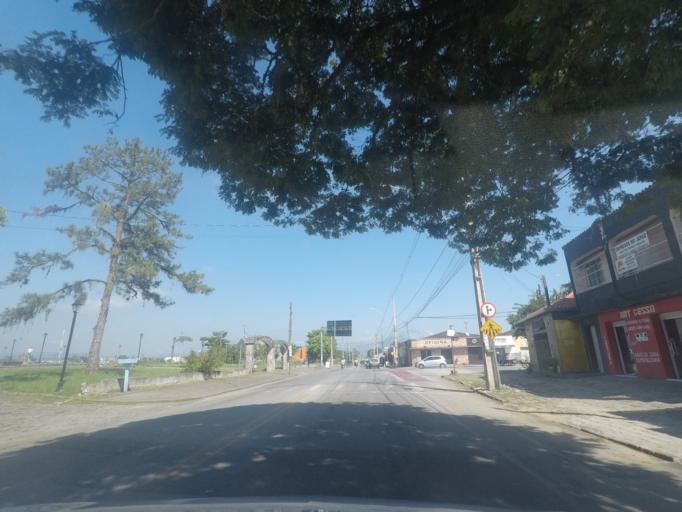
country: BR
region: Parana
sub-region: Paranagua
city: Paranagua
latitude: -25.5368
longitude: -48.5296
